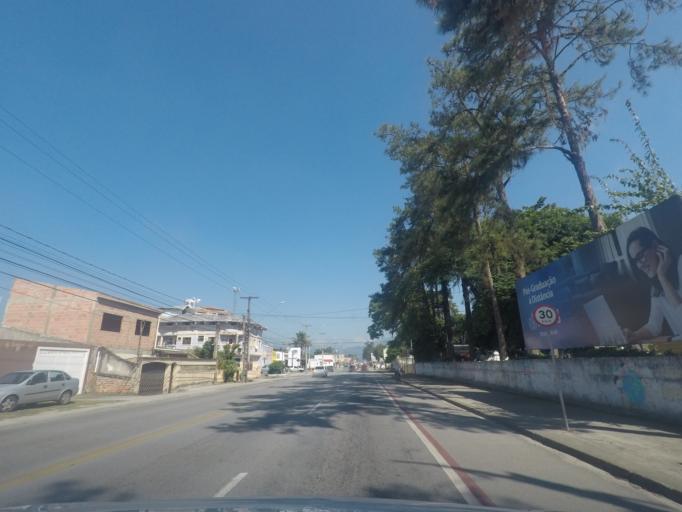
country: BR
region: Parana
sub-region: Paranagua
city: Paranagua
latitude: -25.5491
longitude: -48.5463
